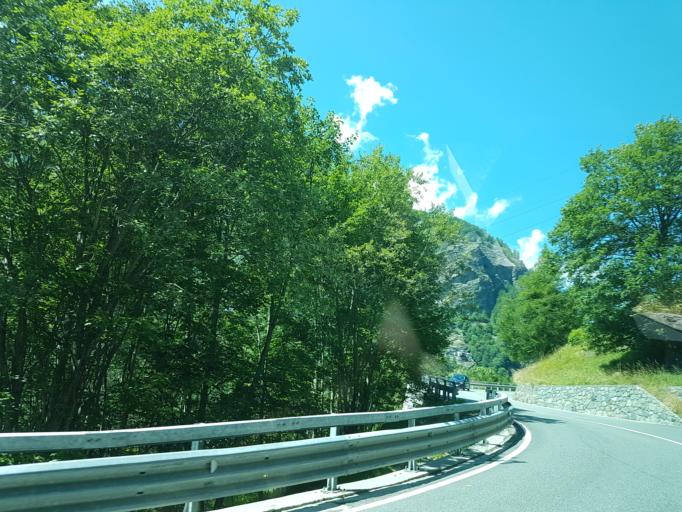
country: IT
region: Aosta Valley
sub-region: Valle d'Aosta
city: Valtournenche
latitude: 45.8677
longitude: 7.6202
